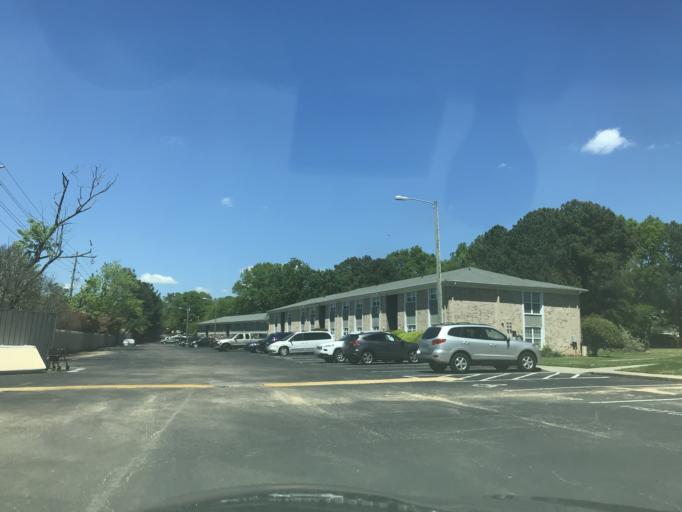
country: US
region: North Carolina
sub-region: Wake County
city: Raleigh
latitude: 35.8454
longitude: -78.5780
